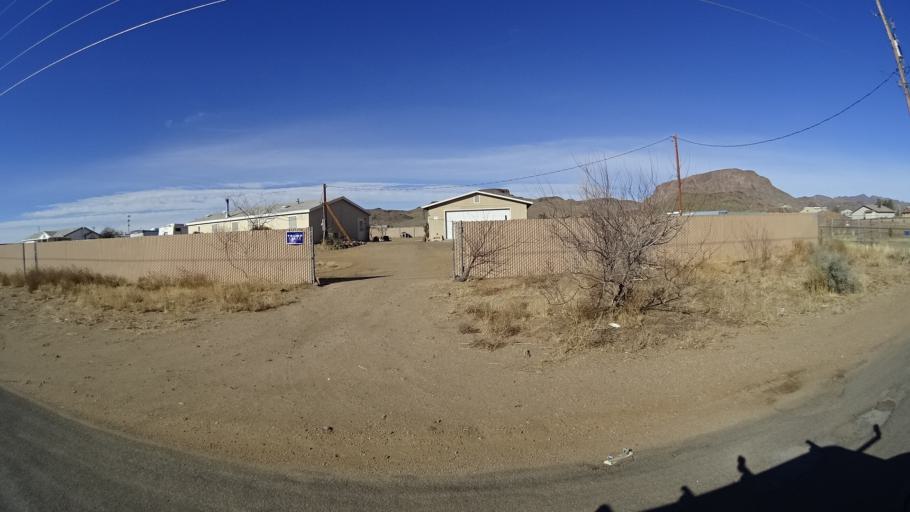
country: US
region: Arizona
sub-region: Mohave County
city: New Kingman-Butler
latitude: 35.2503
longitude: -114.0350
